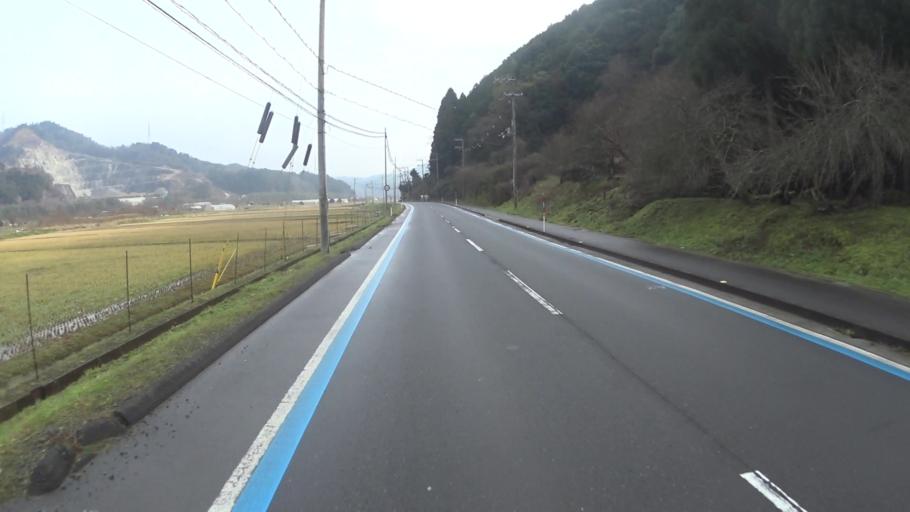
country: JP
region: Kyoto
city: Maizuru
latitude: 35.4259
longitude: 135.2276
